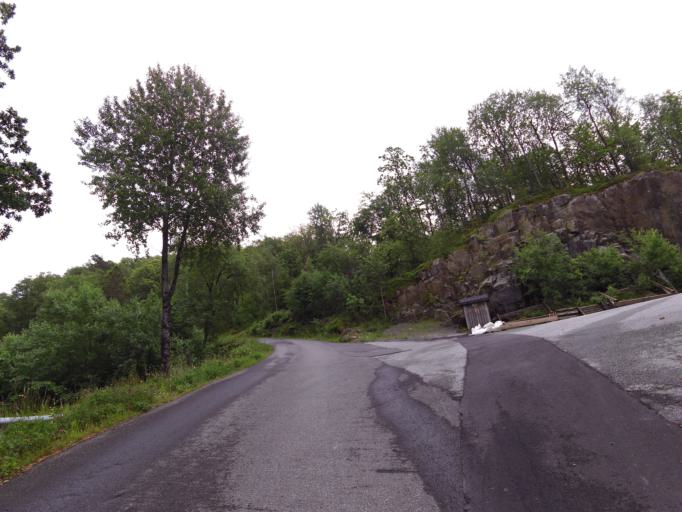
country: NO
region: Vest-Agder
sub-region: Lyngdal
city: Lyngdal
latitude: 58.0994
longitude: 6.9617
